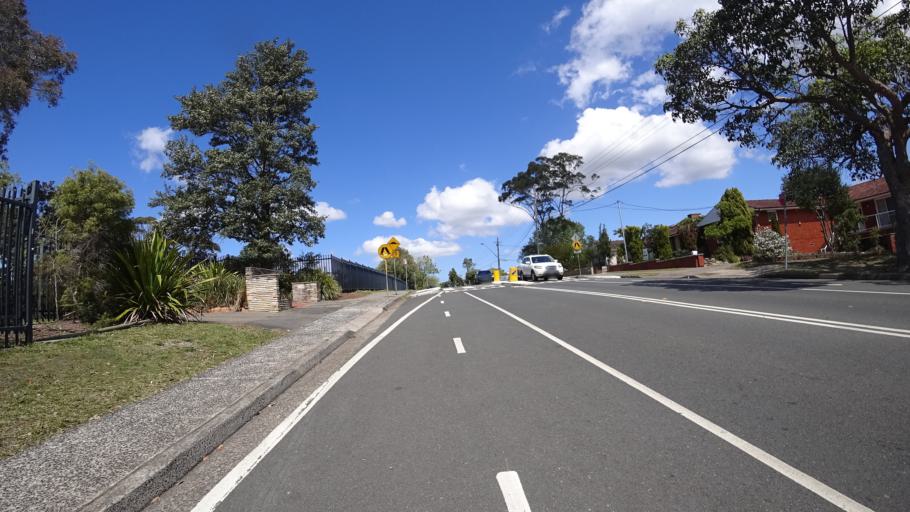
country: AU
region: New South Wales
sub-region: Warringah
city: Forestville
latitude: -33.7609
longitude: 151.2116
